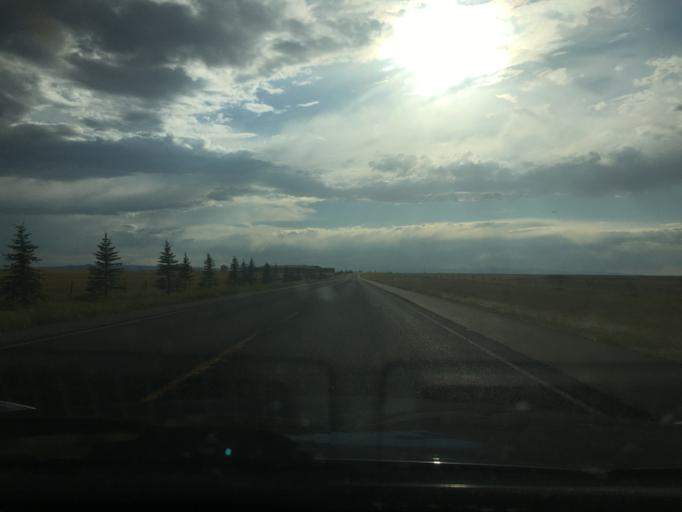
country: US
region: Wyoming
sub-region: Albany County
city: Laramie
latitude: 41.3199
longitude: -105.6441
